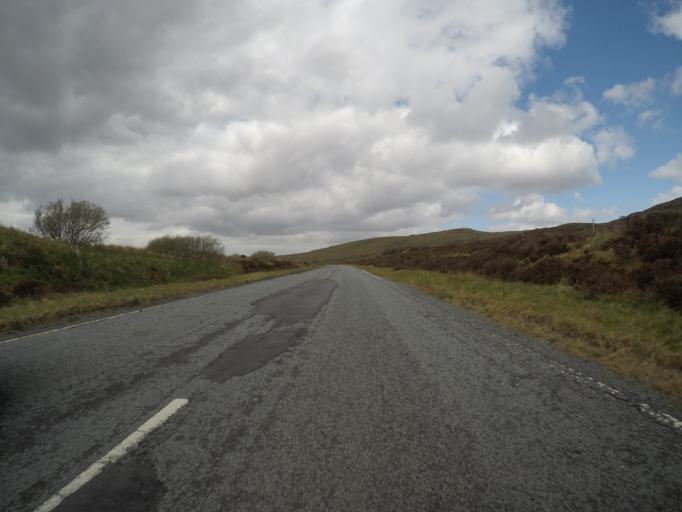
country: GB
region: Scotland
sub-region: Highland
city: Isle of Skye
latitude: 57.3144
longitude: -6.3200
